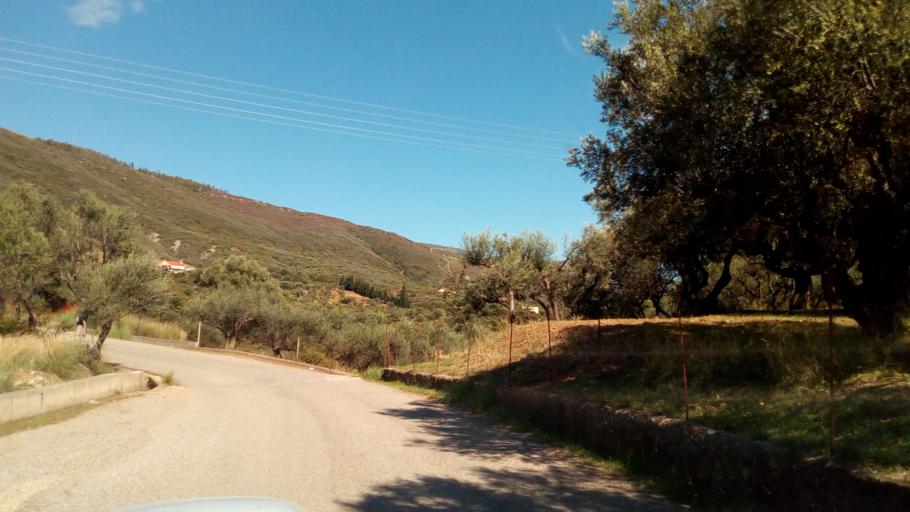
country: GR
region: West Greece
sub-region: Nomos Aitolias kai Akarnanias
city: Antirrio
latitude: 38.3701
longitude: 21.7761
